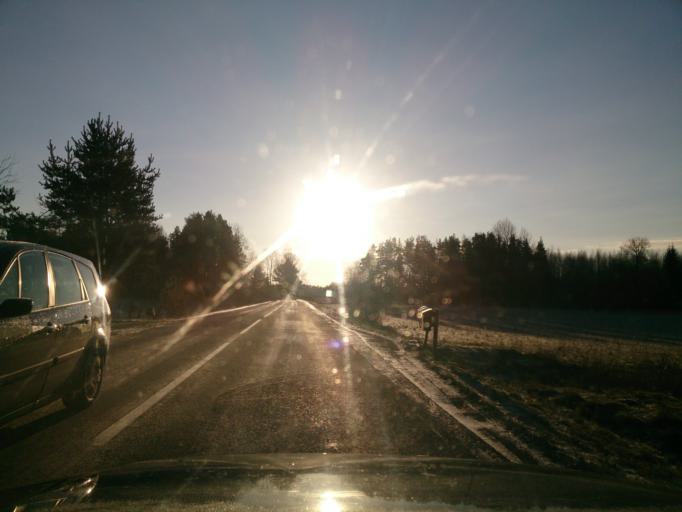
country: SE
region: OEstergoetland
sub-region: Linkopings Kommun
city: Linghem
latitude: 58.4578
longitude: 15.8846
